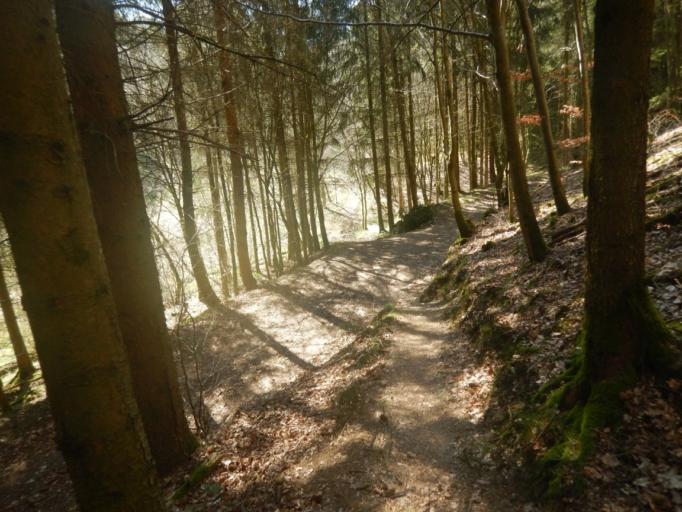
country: LU
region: Diekirch
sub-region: Canton de Wiltz
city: Wiltz
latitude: 49.9554
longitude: 5.9497
